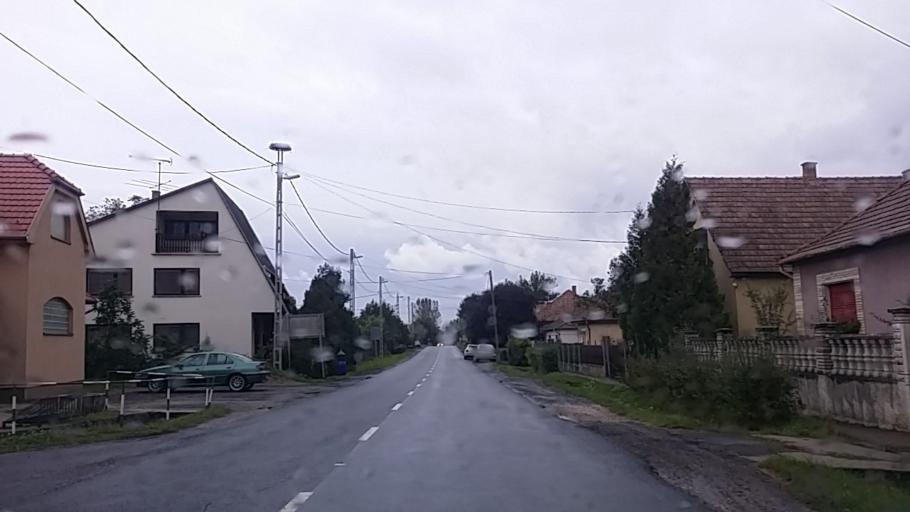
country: HU
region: Komarom-Esztergom
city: Esztergom
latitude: 47.8876
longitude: 18.7759
